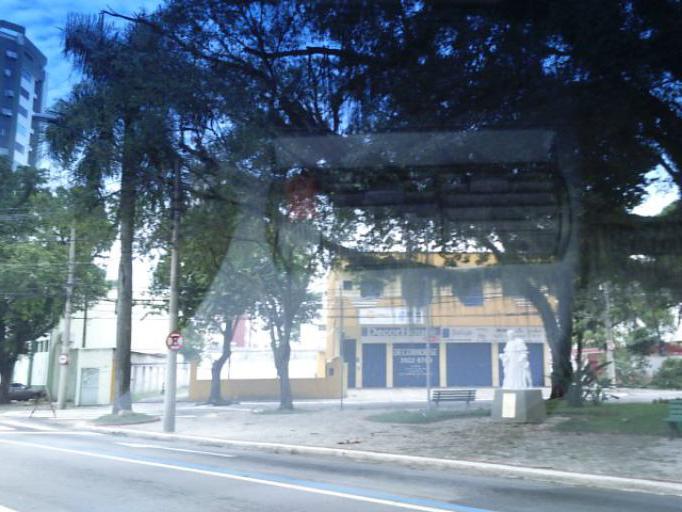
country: BR
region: Sao Paulo
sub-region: Sao Jose Dos Campos
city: Sao Jose dos Campos
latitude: -23.1897
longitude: -45.8873
